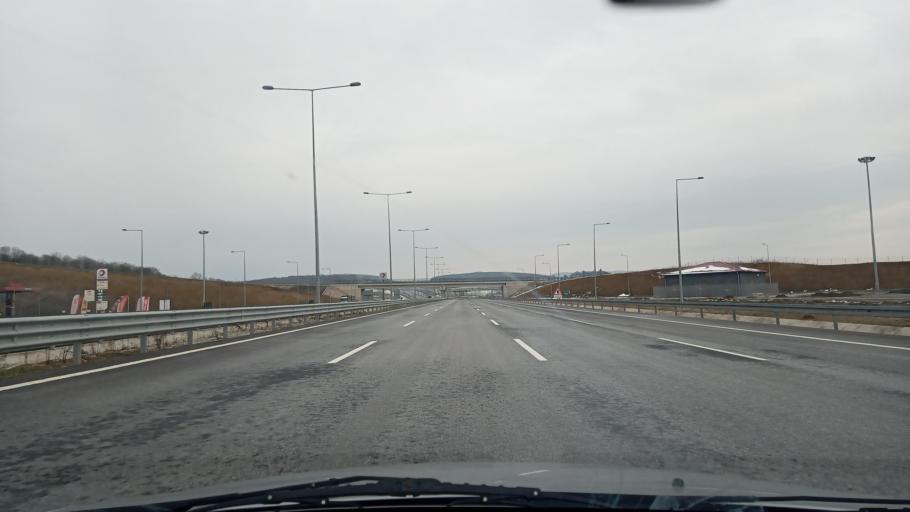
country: TR
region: Kocaeli
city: Derbent
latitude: 40.7952
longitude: 30.0769
